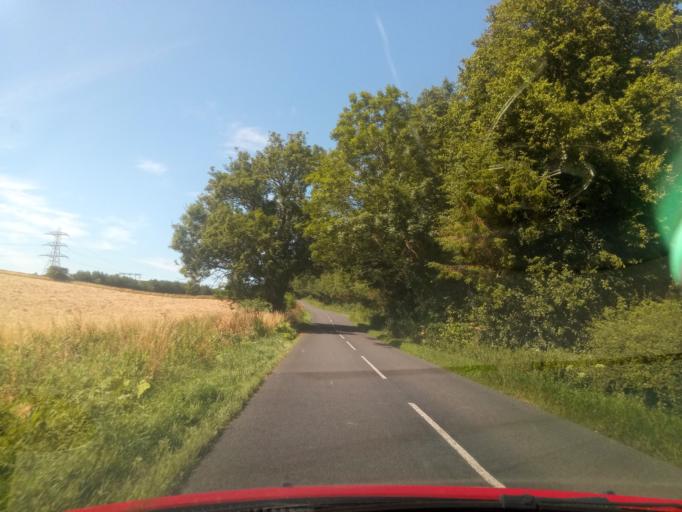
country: GB
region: England
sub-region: Northumberland
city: Wall
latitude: 55.0131
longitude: -2.1564
